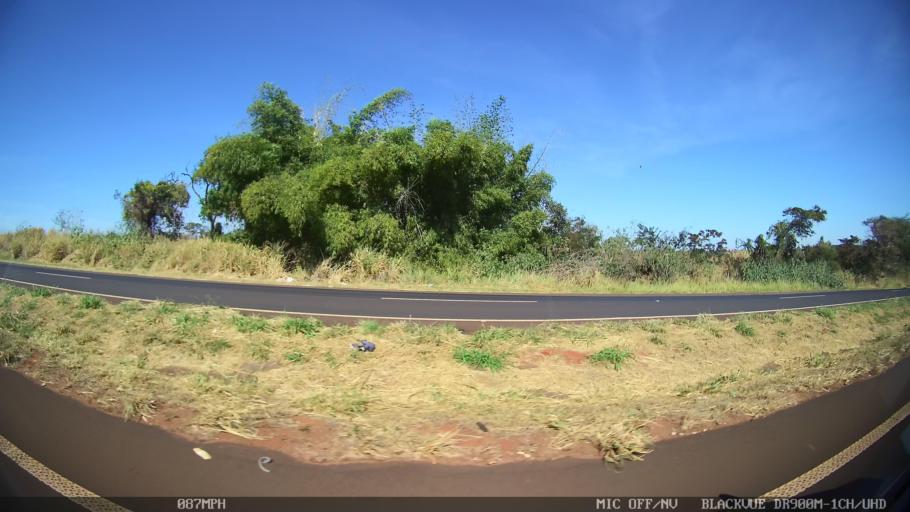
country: BR
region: Sao Paulo
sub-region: Barretos
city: Barretos
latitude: -20.5221
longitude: -48.5807
